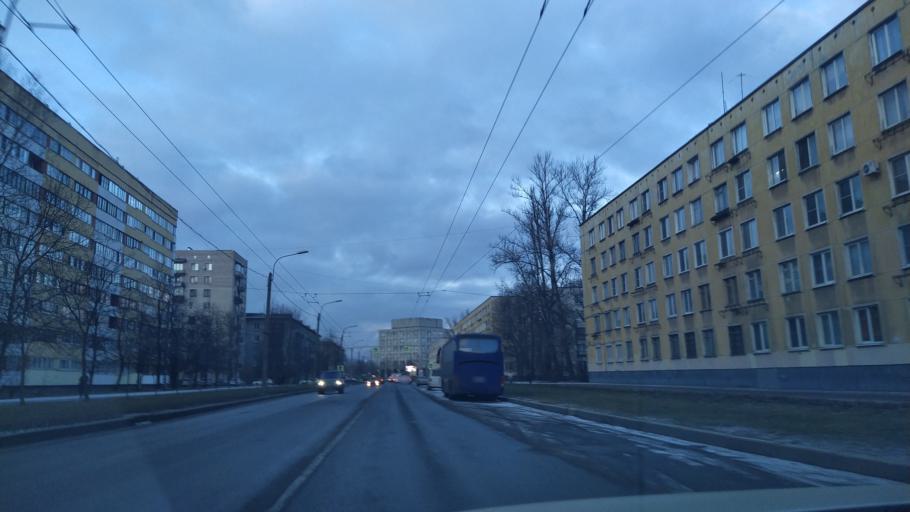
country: RU
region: St.-Petersburg
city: Dachnoye
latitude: 59.8537
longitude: 30.2563
